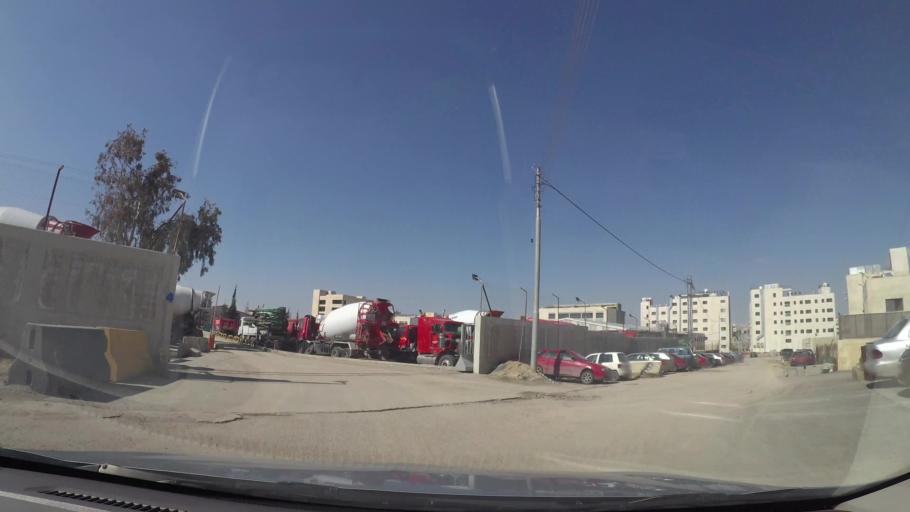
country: JO
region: Amman
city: Al Bunayyat ash Shamaliyah
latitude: 31.9132
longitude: 35.9131
